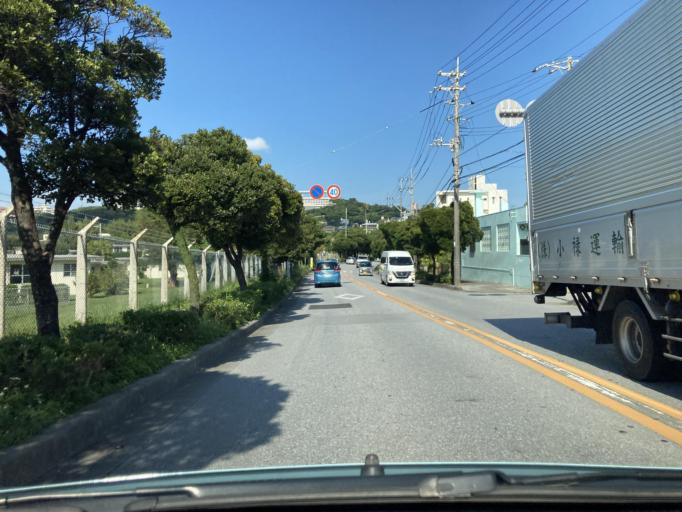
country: JP
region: Okinawa
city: Chatan
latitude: 26.2997
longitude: 127.7889
